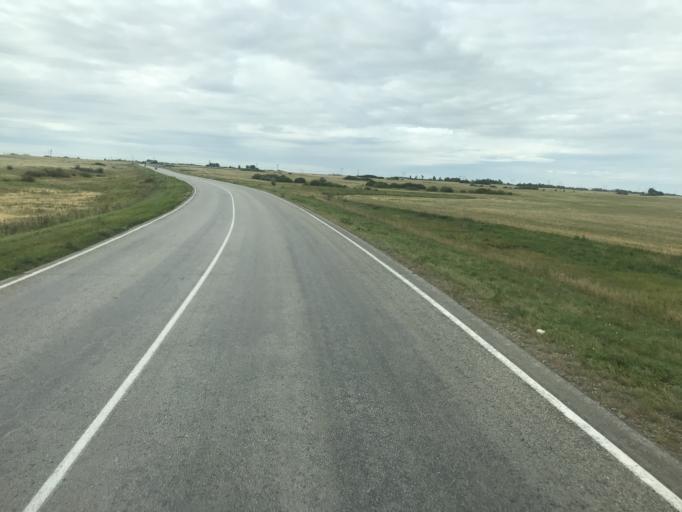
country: RU
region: Chelyabinsk
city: Bobrovka
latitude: 53.9857
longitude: 61.6985
